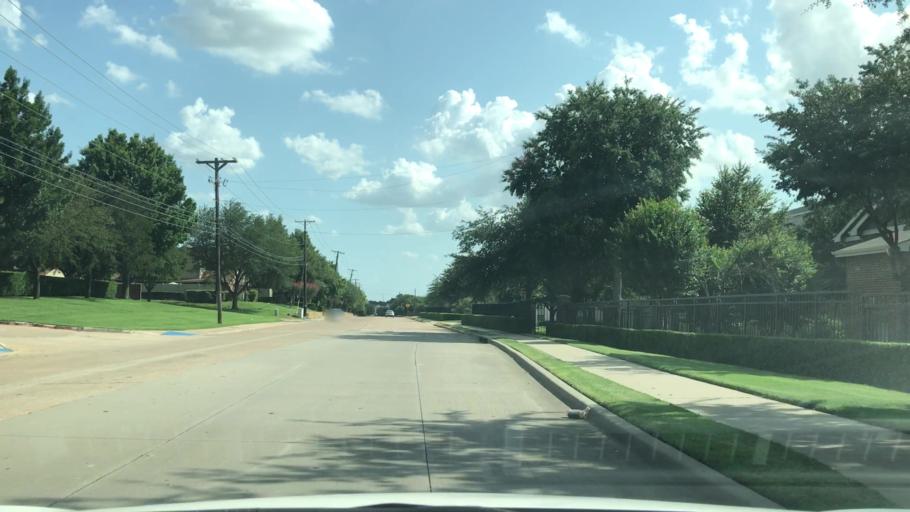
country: US
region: Texas
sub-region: Dallas County
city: Addison
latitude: 32.9732
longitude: -96.8515
